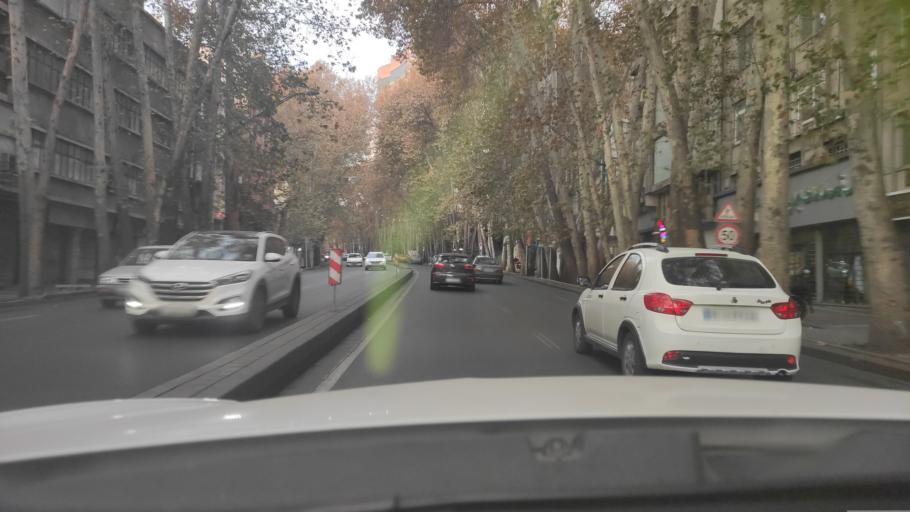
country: IR
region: Tehran
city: Tajrish
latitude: 35.8069
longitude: 51.4268
